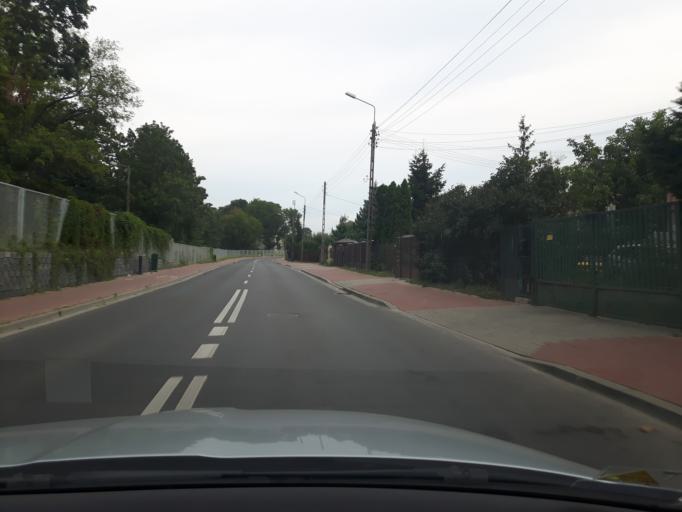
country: PL
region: Masovian Voivodeship
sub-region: Powiat wolominski
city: Zabki
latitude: 52.3009
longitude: 21.1074
